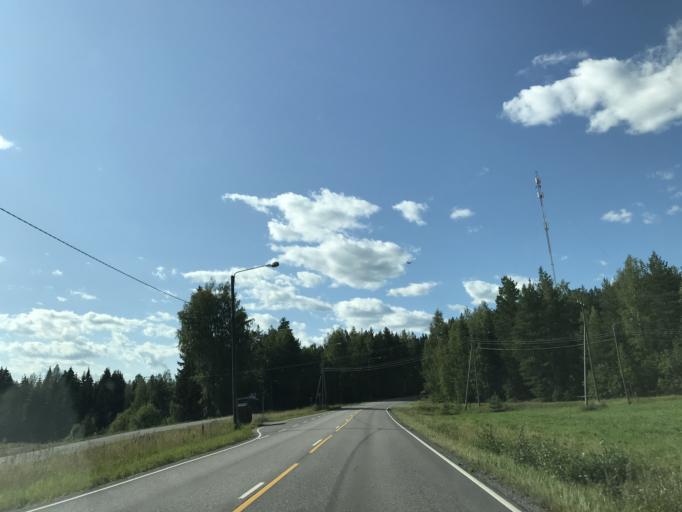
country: FI
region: Uusimaa
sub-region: Helsinki
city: Nurmijaervi
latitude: 60.4048
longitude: 24.9042
